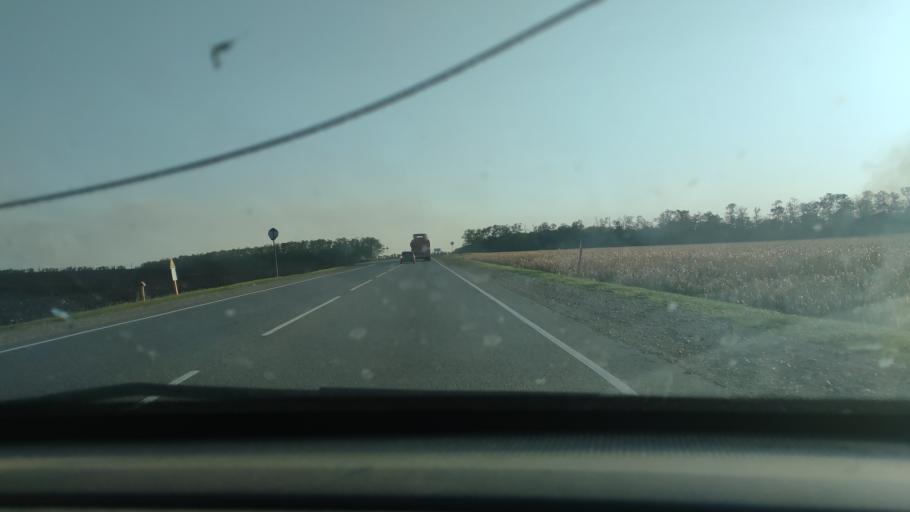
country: RU
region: Krasnodarskiy
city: Kanevskaya
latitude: 46.0423
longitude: 38.9870
